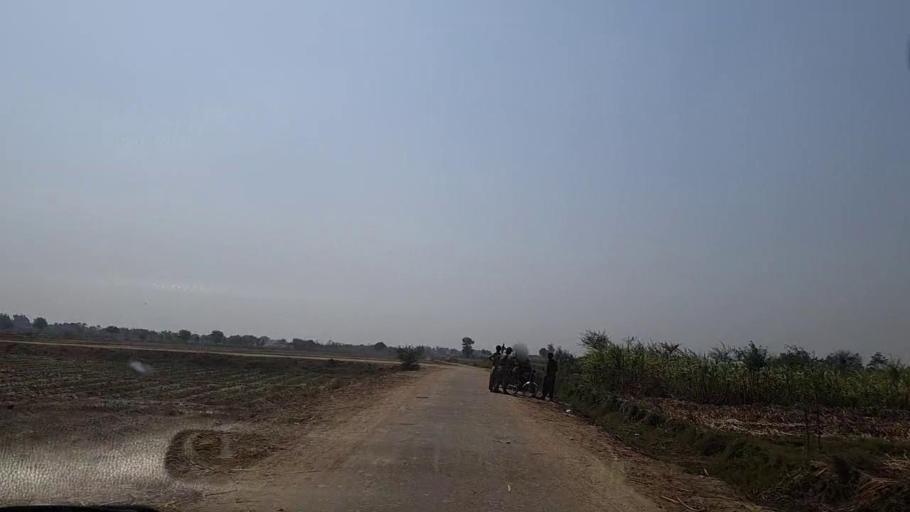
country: PK
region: Sindh
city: Mirpur Khas
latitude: 25.4832
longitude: 69.1937
